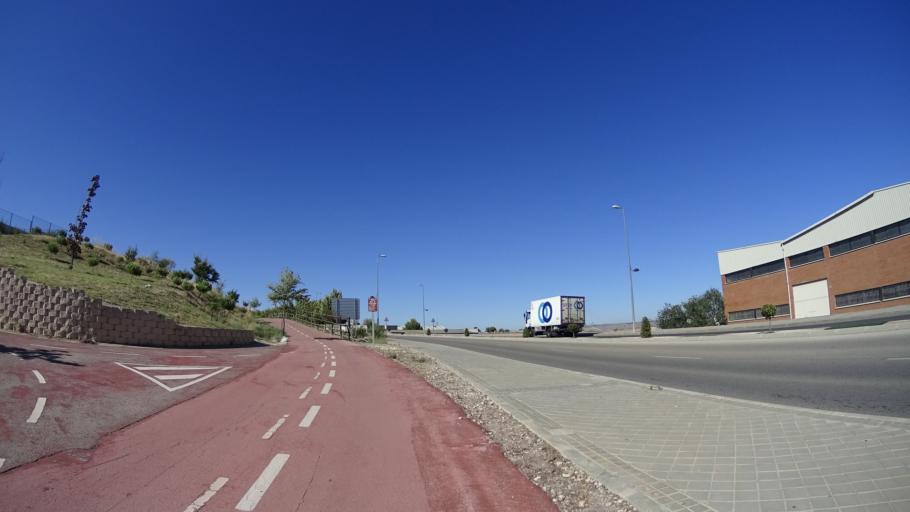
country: ES
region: Madrid
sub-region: Provincia de Madrid
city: Arganda
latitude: 40.3029
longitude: -3.4531
